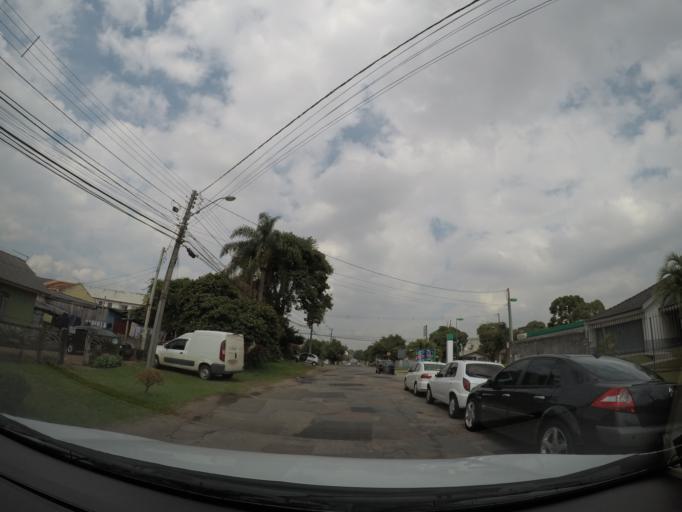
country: BR
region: Parana
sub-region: Sao Jose Dos Pinhais
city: Sao Jose dos Pinhais
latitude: -25.4989
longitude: -49.2499
